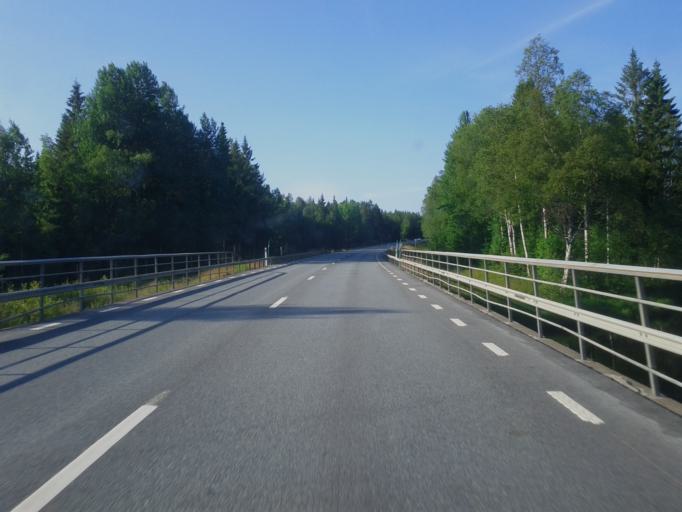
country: SE
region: Vaesterbotten
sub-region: Robertsfors Kommun
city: Robertsfors
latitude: 64.0332
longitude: 20.8419
